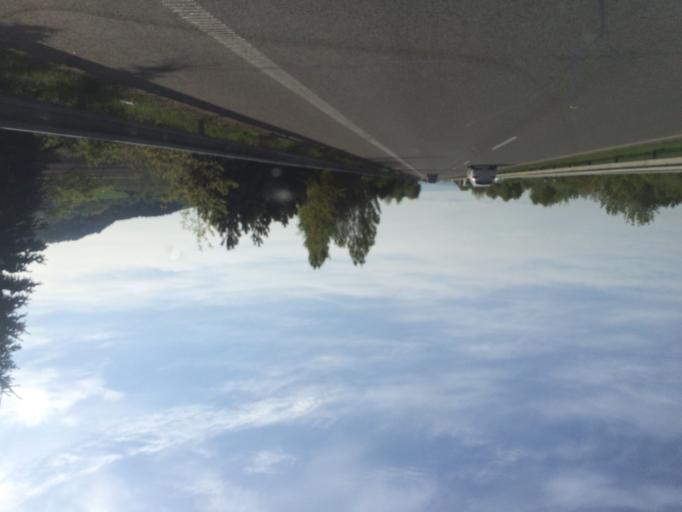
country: CZ
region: Central Bohemia
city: Mnichovo Hradiste
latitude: 50.5333
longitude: 15.0163
